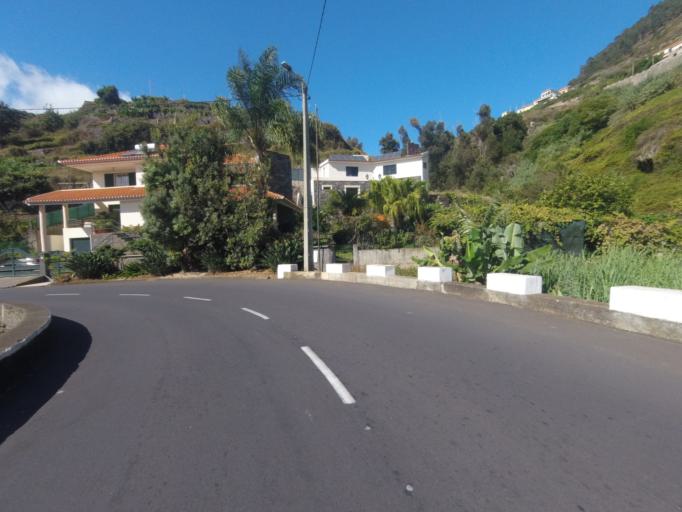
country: PT
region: Madeira
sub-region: Ribeira Brava
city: Campanario
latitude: 32.6750
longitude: -17.0237
